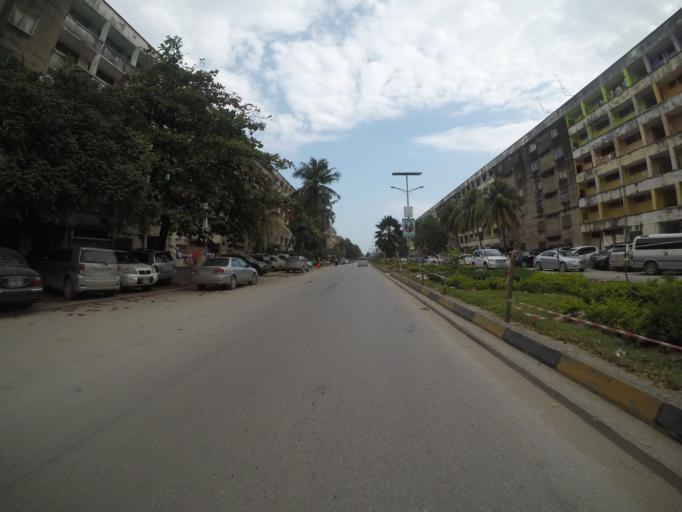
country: TZ
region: Zanzibar Urban/West
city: Zanzibar
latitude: -6.1660
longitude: 39.1990
